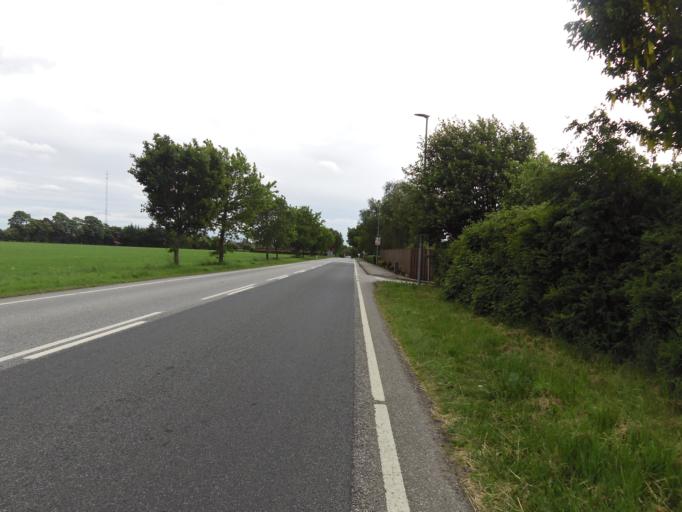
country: DK
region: South Denmark
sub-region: Vejen Kommune
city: Rodding
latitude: 55.3339
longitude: 9.0569
